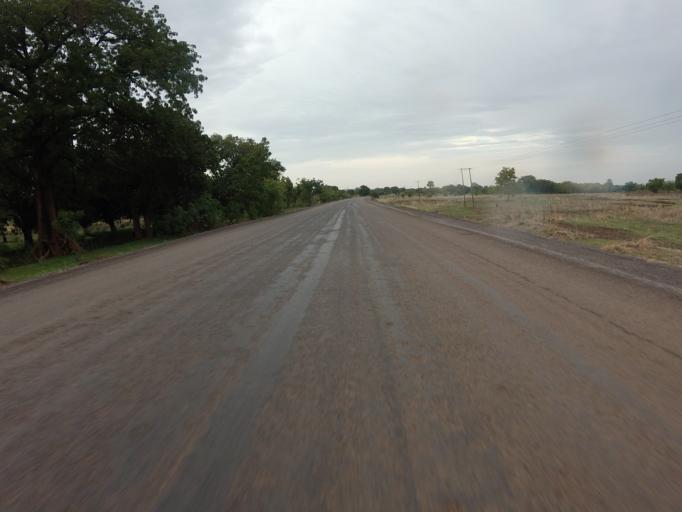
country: GH
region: Upper East
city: Bolgatanga
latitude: 10.8633
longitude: -0.6604
